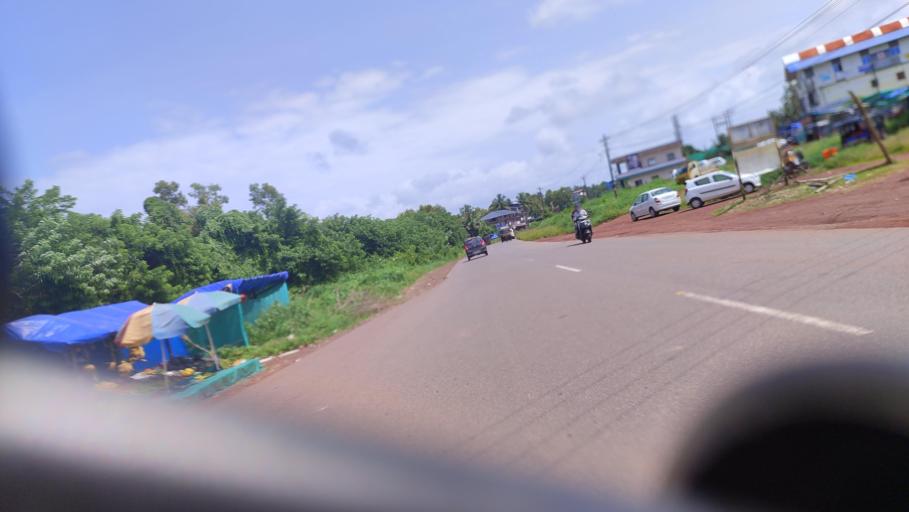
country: IN
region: Kerala
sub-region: Kasaragod District
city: Kannangad
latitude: 12.4021
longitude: 75.0970
